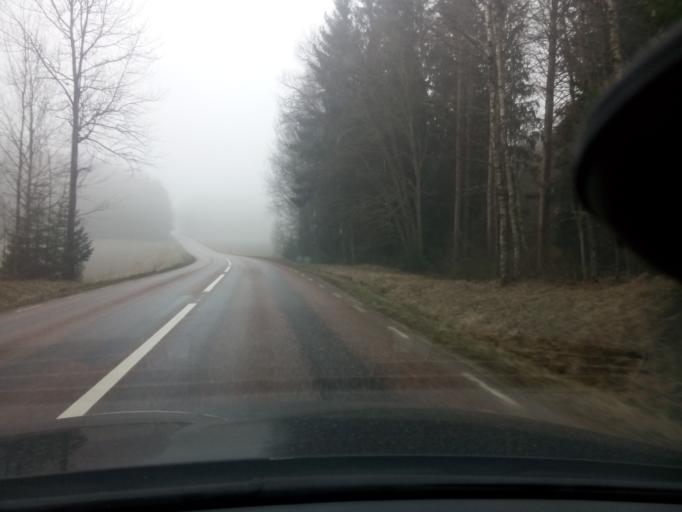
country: SE
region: Soedermanland
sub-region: Nykopings Kommun
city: Nykoping
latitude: 58.8301
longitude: 17.0746
